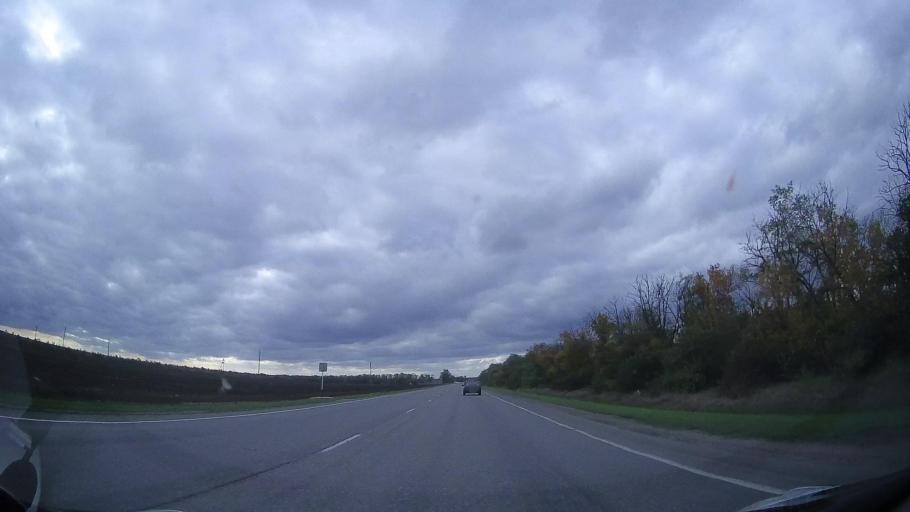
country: RU
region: Rostov
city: Zernograd
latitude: 46.8149
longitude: 40.2773
